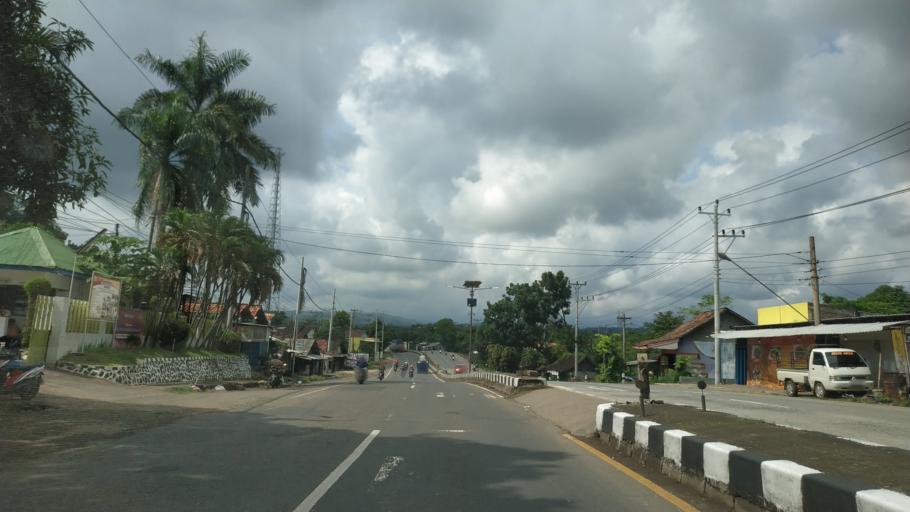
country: ID
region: Central Java
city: Pekalongan
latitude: -6.9445
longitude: 109.7768
